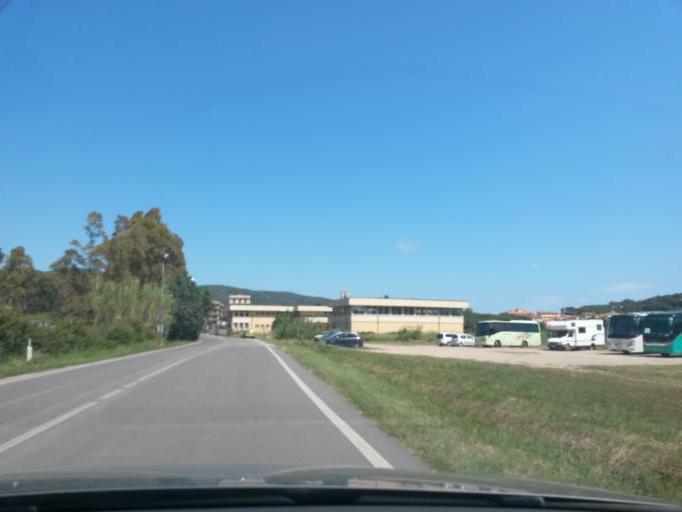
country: IT
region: Tuscany
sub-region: Provincia di Livorno
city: Campo nell'Elba
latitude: 42.7456
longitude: 10.2291
